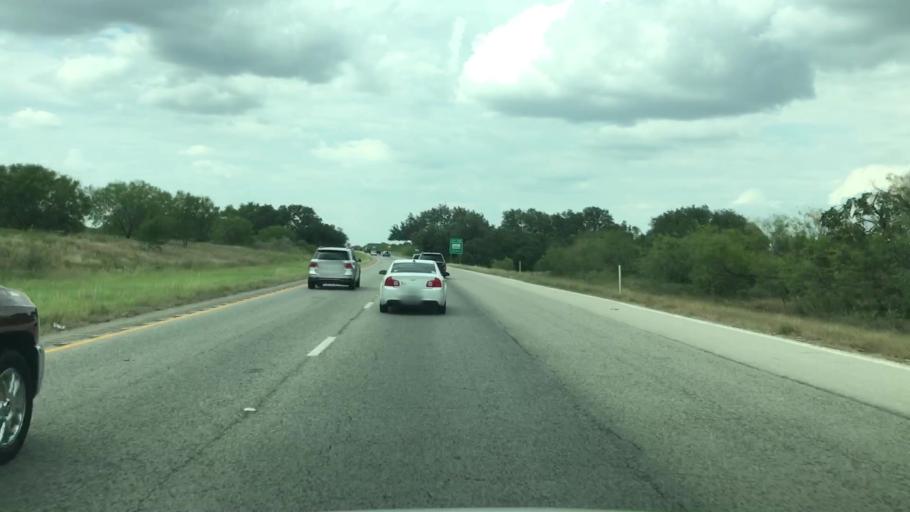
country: US
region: Texas
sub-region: Atascosa County
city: Pleasanton
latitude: 29.0405
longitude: -98.4314
